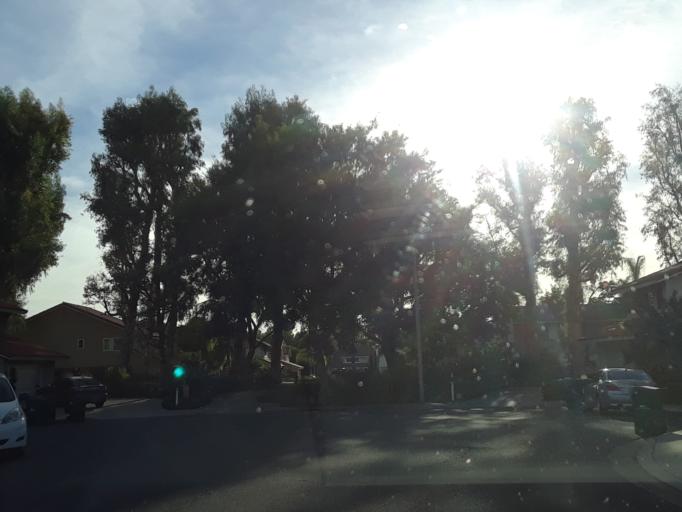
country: US
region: California
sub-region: Orange County
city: North Tustin
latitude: 33.7214
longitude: -117.7665
